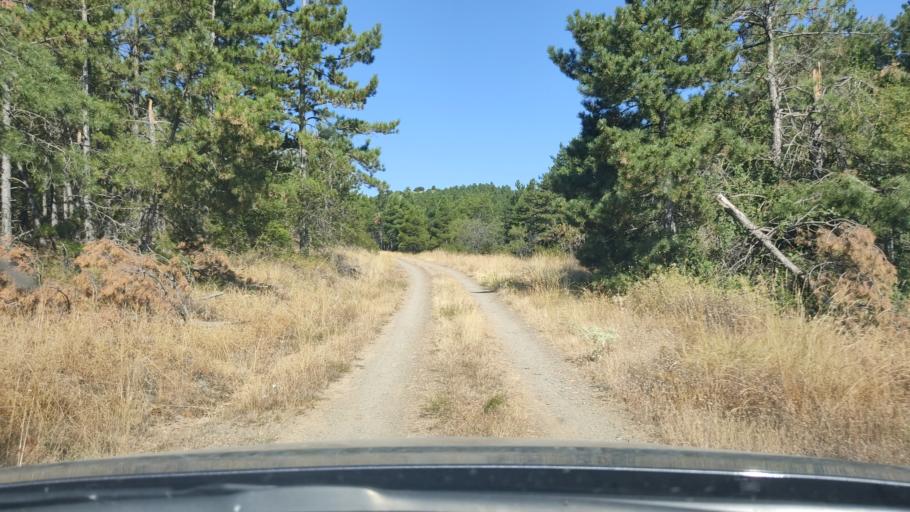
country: ES
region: Aragon
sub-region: Provincia de Teruel
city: Monforte de Moyuela
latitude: 41.0407
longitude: -1.0379
